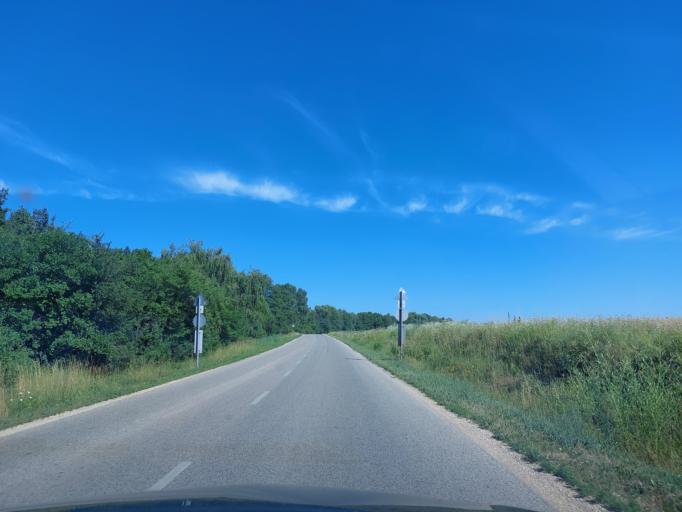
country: HU
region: Veszprem
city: Ajka
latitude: 47.0818
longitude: 17.5230
